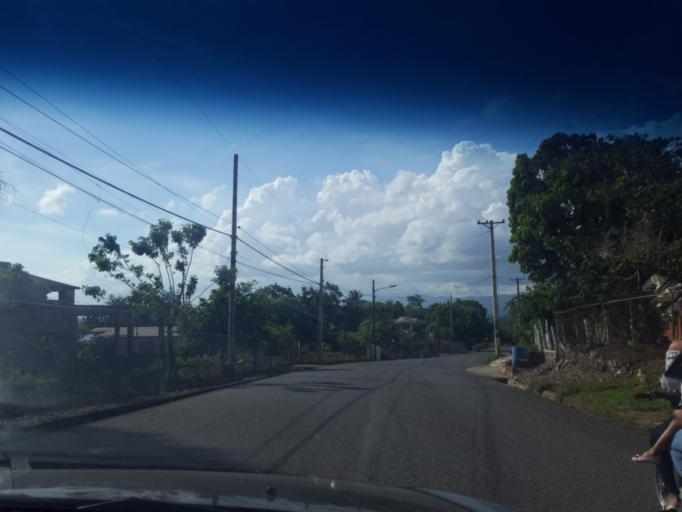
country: DO
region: Santiago
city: Licey al Medio
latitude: 19.3715
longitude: -70.6079
